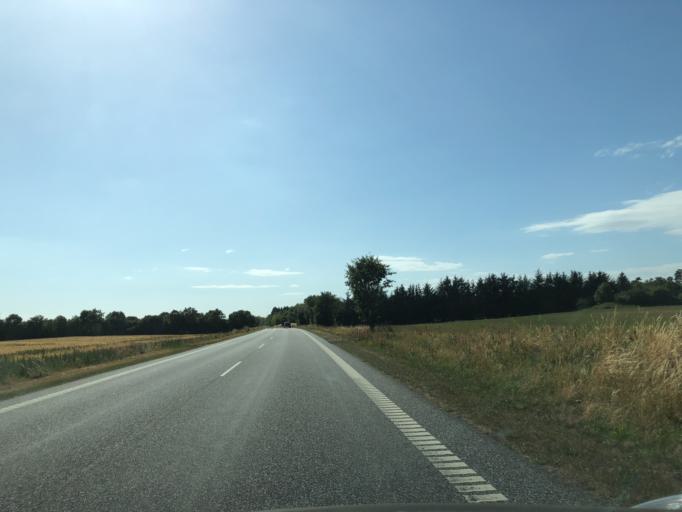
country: DK
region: North Denmark
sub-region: Vesthimmerland Kommune
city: Alestrup
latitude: 56.6123
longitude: 9.3830
